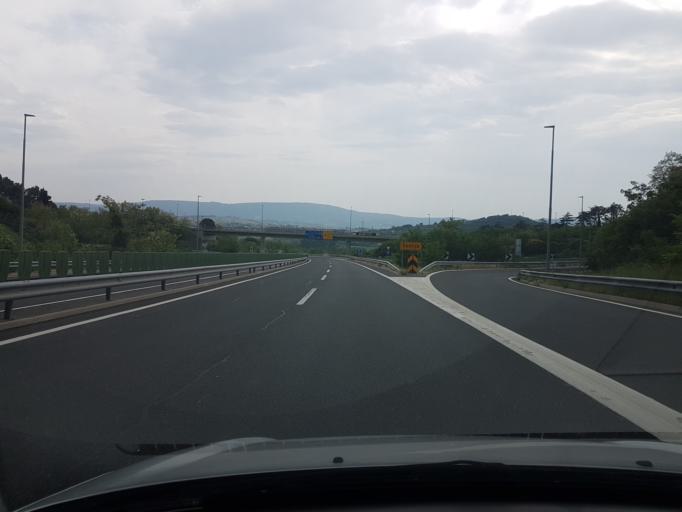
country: SI
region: Koper-Capodistria
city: Spodnje Skofije
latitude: 45.5679
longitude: 13.7848
